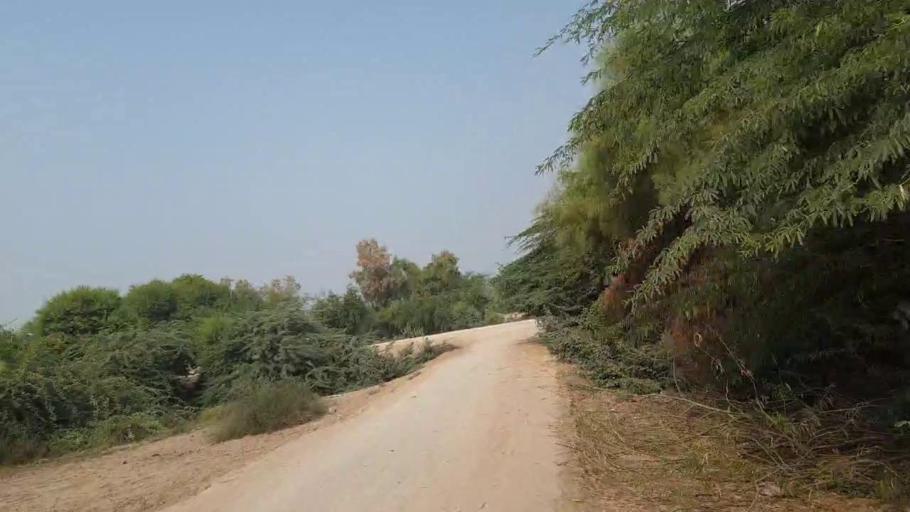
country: PK
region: Sindh
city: Bhan
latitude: 26.5413
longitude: 67.7012
